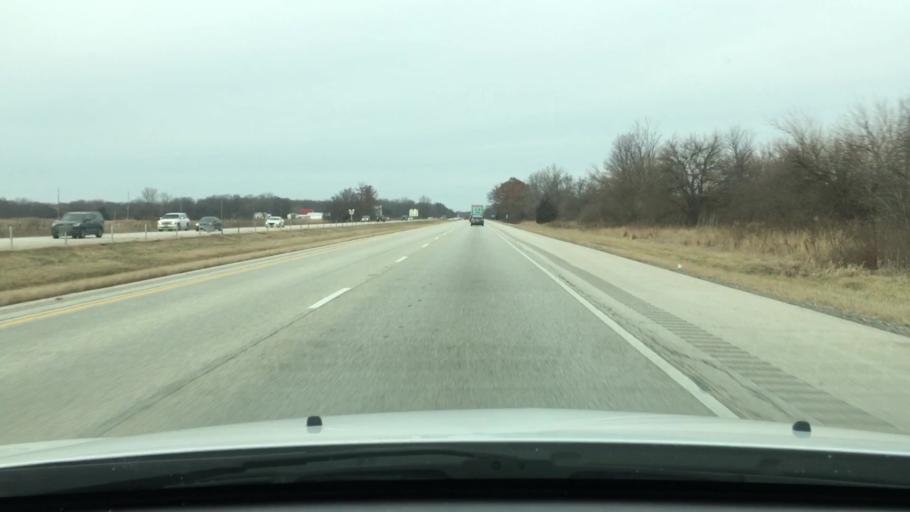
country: US
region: Illinois
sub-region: Sangamon County
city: Grandview
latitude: 39.8490
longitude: -89.5943
